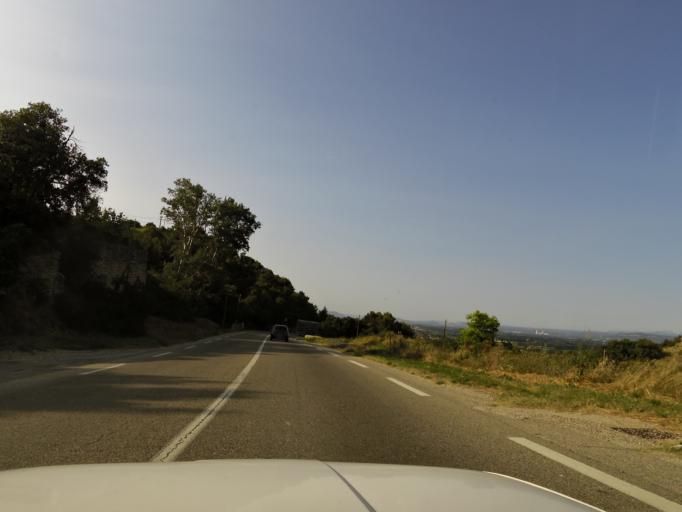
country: FR
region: Languedoc-Roussillon
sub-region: Departement du Gard
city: Saint-Alexandre
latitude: 44.2151
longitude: 4.6332
